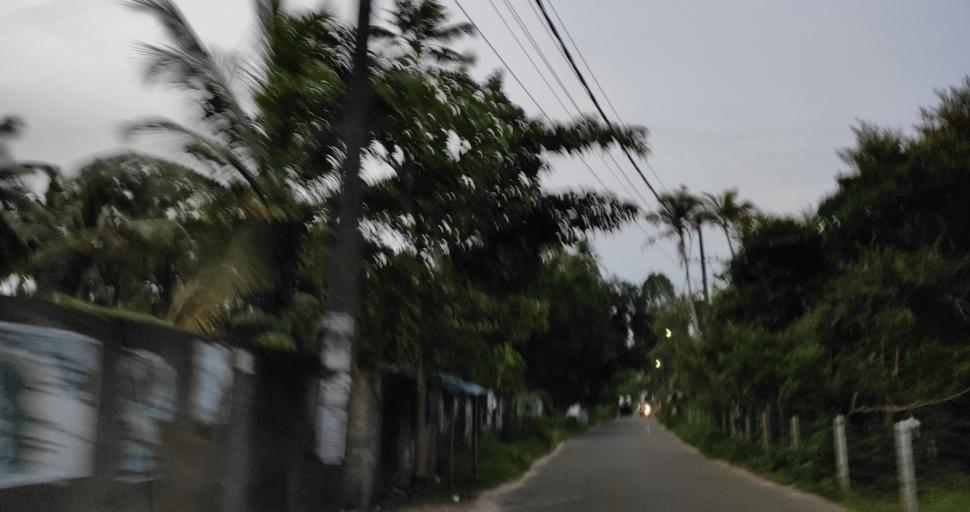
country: IN
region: Kerala
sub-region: Alappuzha
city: Vayalar
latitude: 9.6814
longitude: 76.3184
